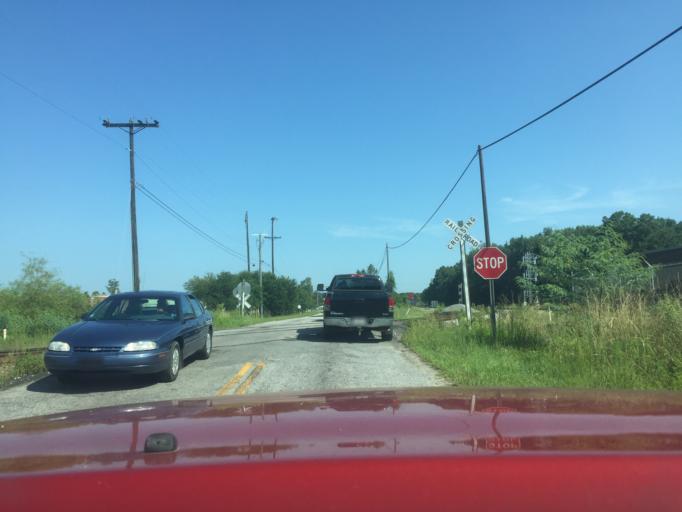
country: US
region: Georgia
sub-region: Chatham County
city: Garden City
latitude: 32.0762
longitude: -81.1441
